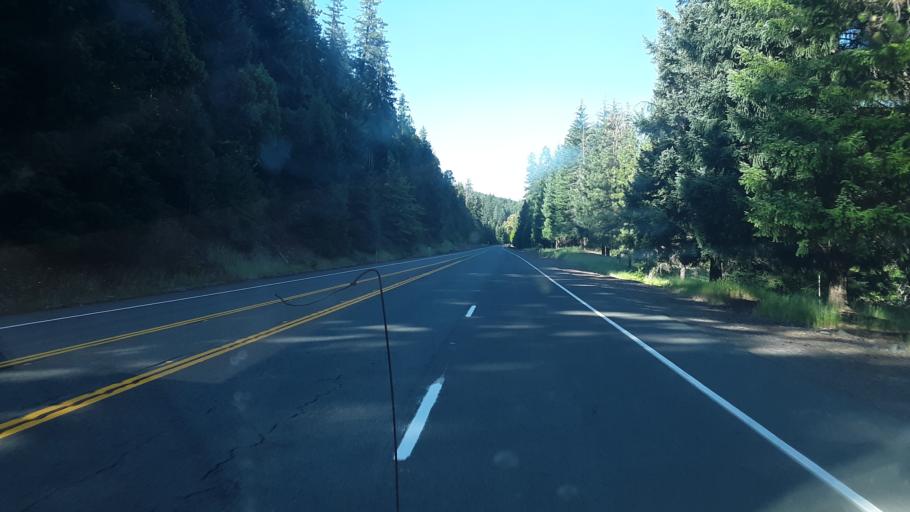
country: US
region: Oregon
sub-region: Jackson County
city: Shady Cove
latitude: 42.6814
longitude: -122.6151
